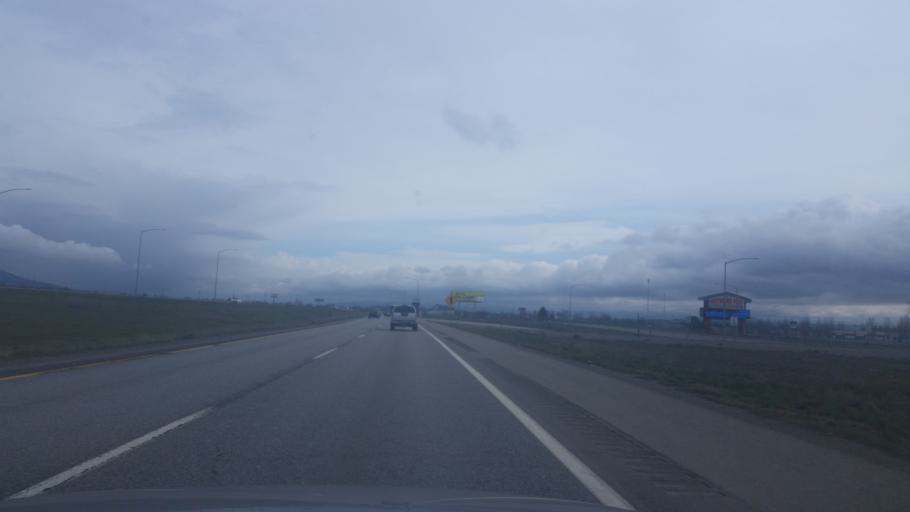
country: US
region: Washington
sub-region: Spokane County
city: Otis Orchards-East Farms
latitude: 47.7020
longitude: -117.0175
